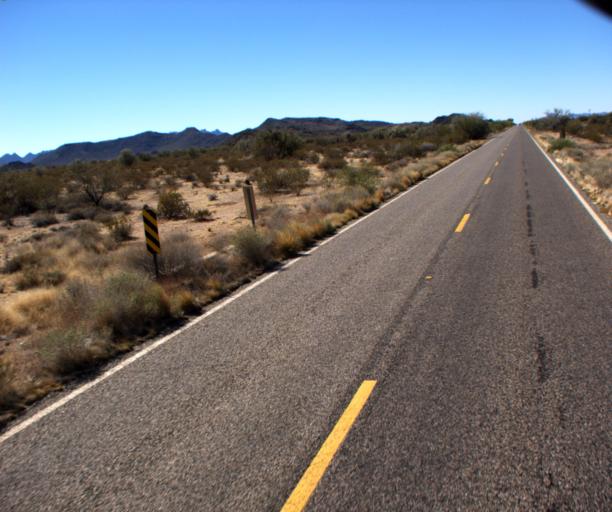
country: US
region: Arizona
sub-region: Pima County
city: Ajo
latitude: 32.2468
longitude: -112.7472
